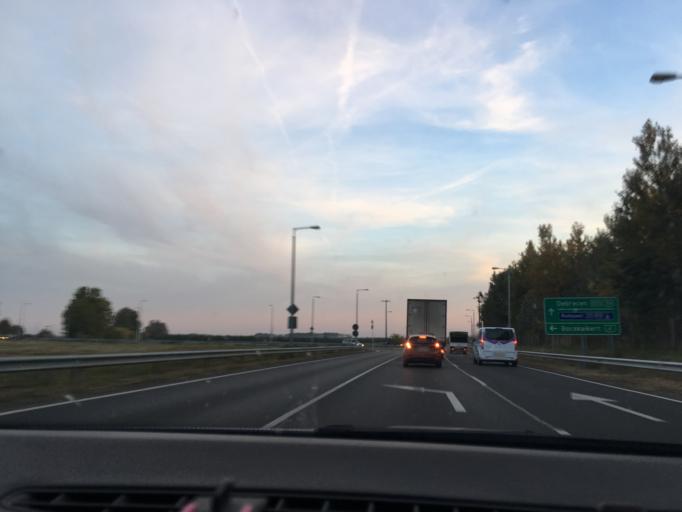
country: HU
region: Hajdu-Bihar
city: Hajduhadhaz
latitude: 47.6670
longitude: 21.6520
